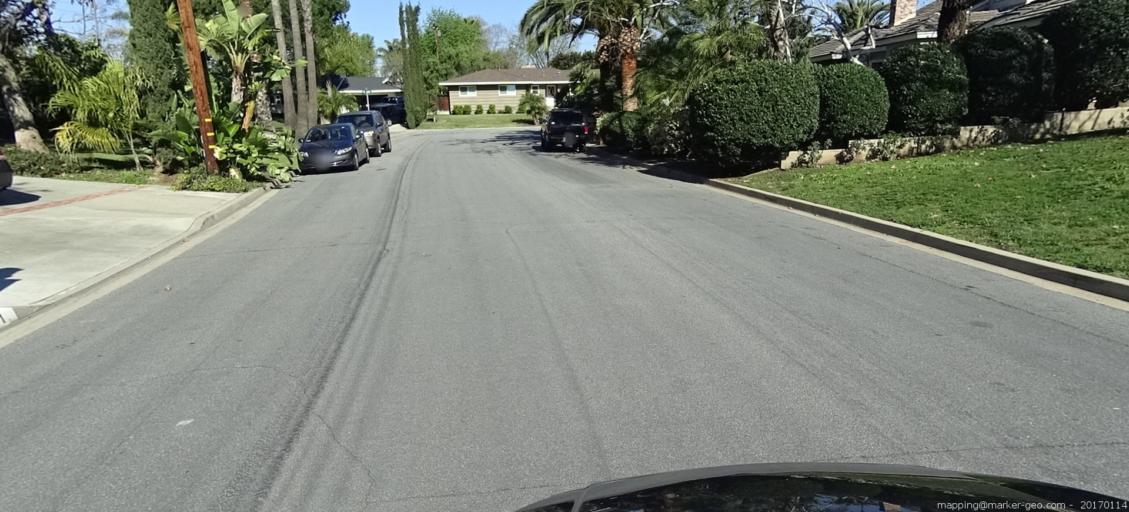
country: US
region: California
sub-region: Orange County
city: North Tustin
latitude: 33.7647
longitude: -117.8051
